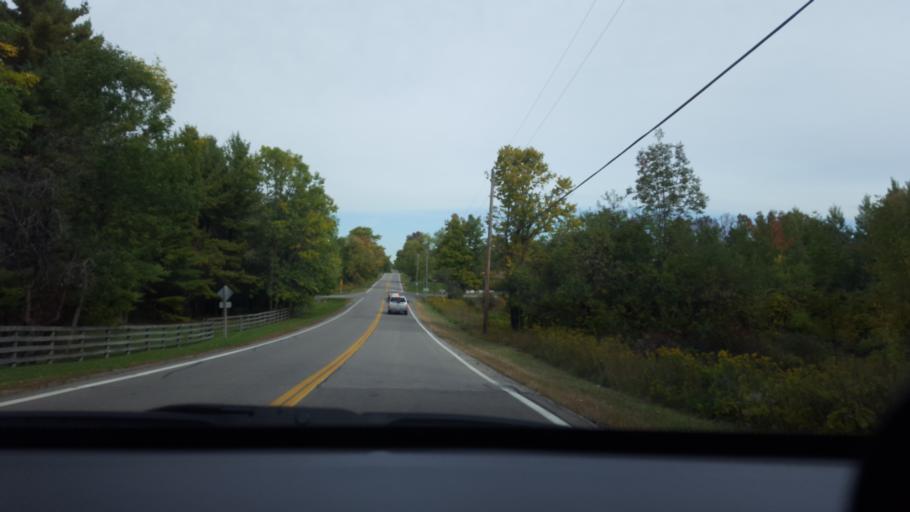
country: CA
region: Ontario
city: Newmarket
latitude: 43.9637
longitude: -79.5380
